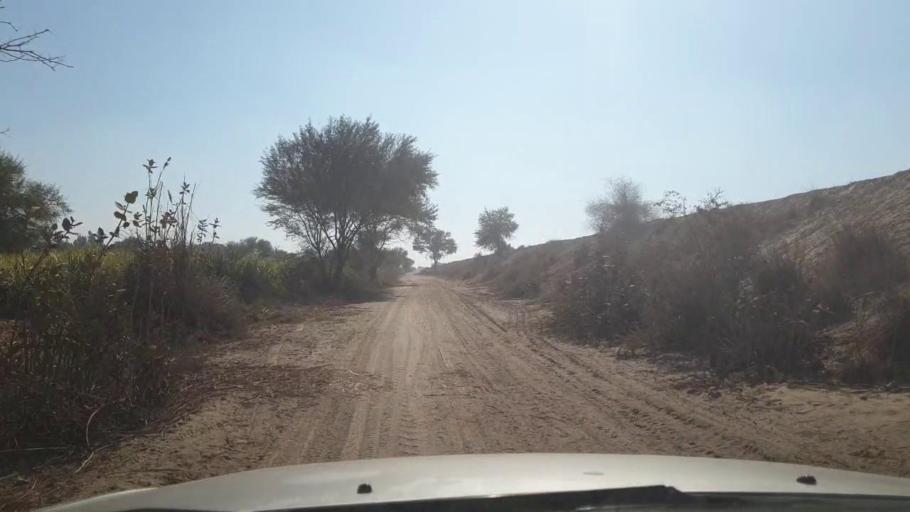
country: PK
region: Sindh
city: Ghotki
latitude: 28.0295
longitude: 69.2106
